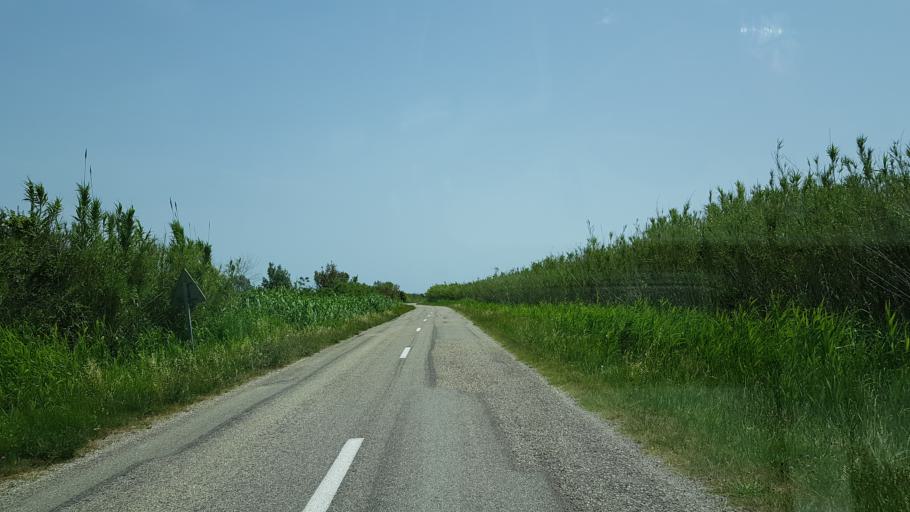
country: FR
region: Provence-Alpes-Cote d'Azur
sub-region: Departement des Bouches-du-Rhone
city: Port-Saint-Louis-du-Rhone
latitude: 43.4413
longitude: 4.6787
